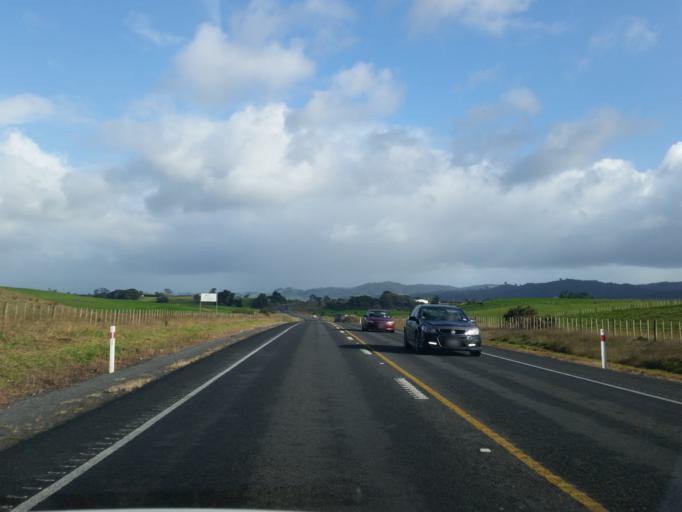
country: NZ
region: Waikato
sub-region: Waikato District
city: Te Kauwhata
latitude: -37.2209
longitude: 175.1363
